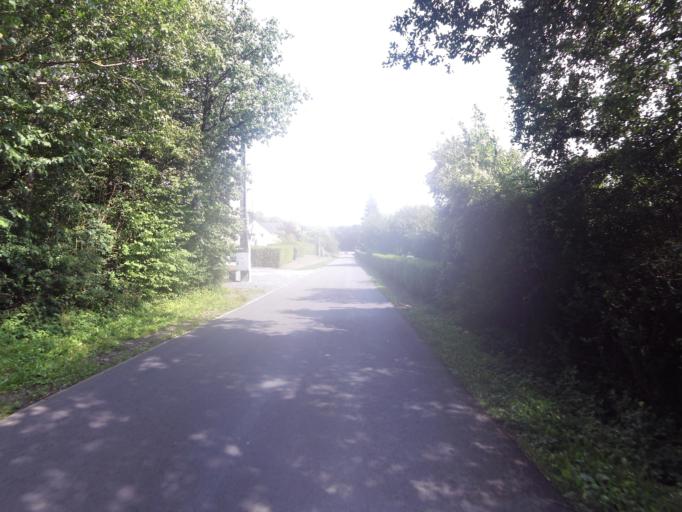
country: BE
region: Wallonia
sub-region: Province du Luxembourg
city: Durbuy
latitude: 50.3450
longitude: 5.4681
